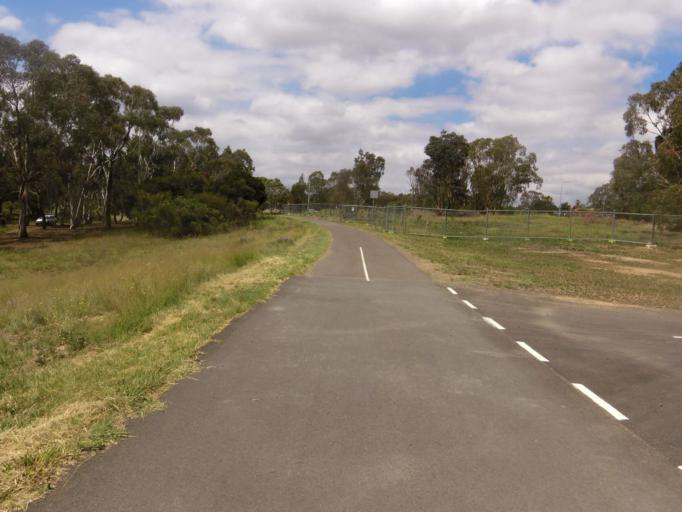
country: AU
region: Australian Capital Territory
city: Macarthur
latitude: -35.4184
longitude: 149.0737
